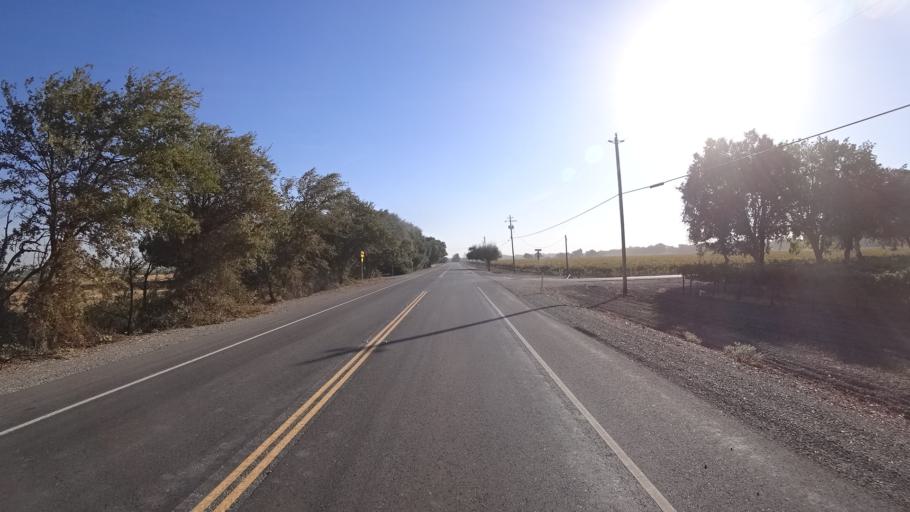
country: US
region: California
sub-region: Sacramento County
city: Parkway
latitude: 38.4144
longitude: -121.5509
